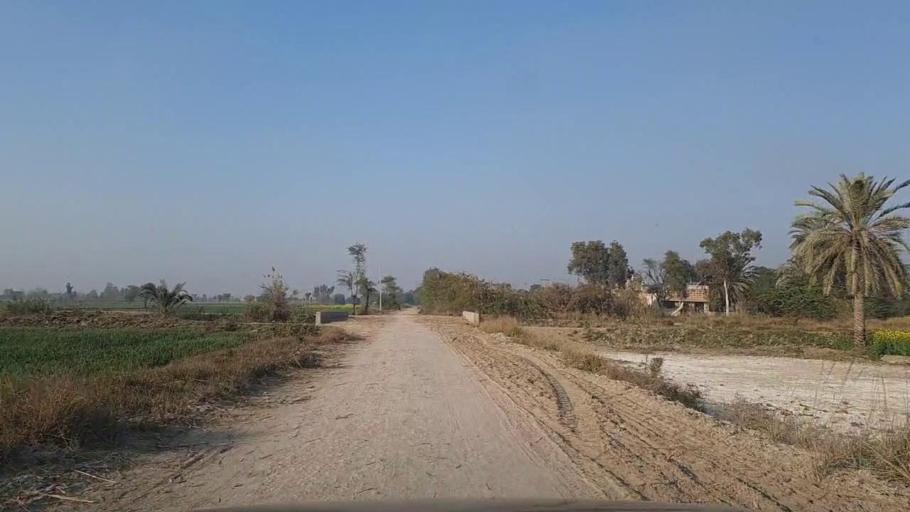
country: PK
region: Sindh
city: Daur
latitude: 26.4619
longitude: 68.4380
